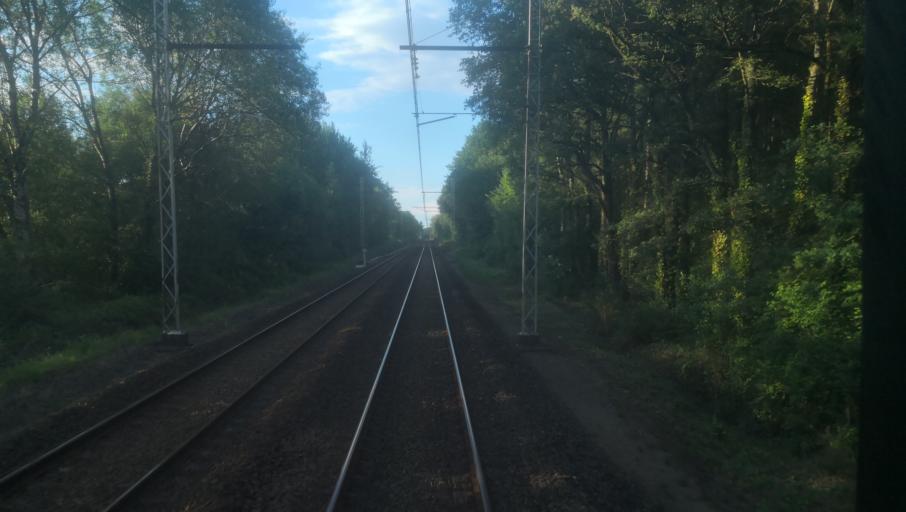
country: FR
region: Centre
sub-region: Departement de l'Indre
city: Luant
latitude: 46.7285
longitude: 1.5861
